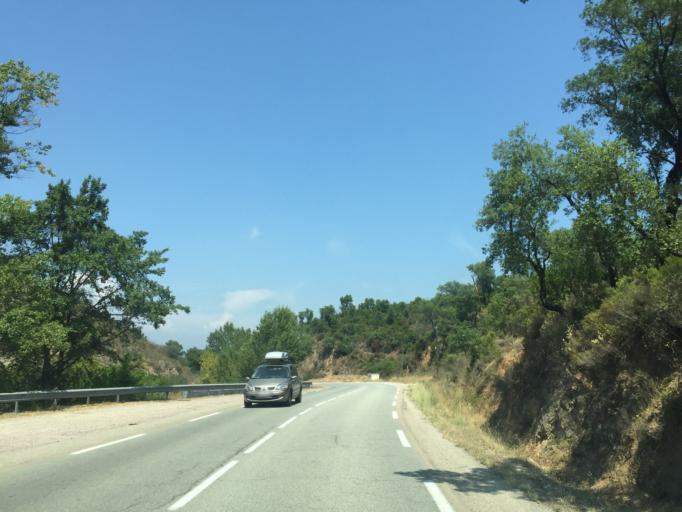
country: FR
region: Provence-Alpes-Cote d'Azur
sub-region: Departement du Var
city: Roquebrune-sur-Argens
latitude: 43.3867
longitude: 6.6764
